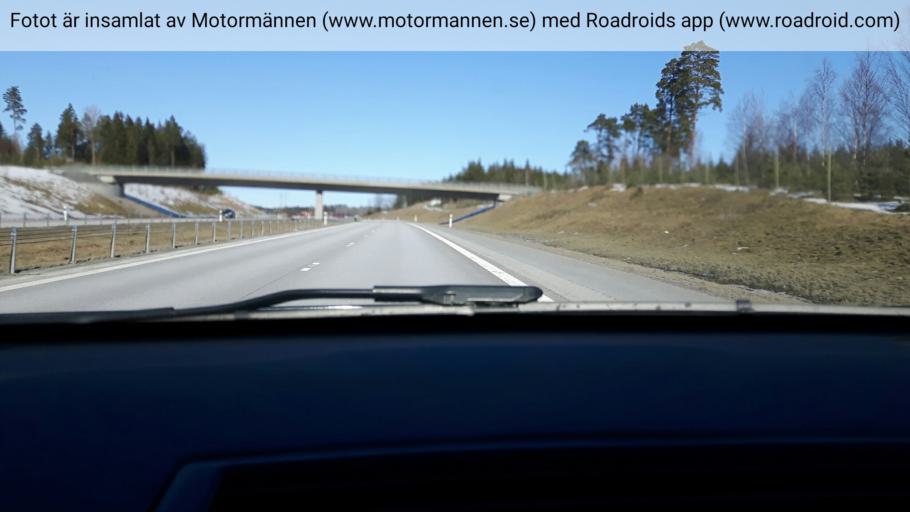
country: SE
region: Uppsala
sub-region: Uppsala Kommun
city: Storvreta
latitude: 59.9652
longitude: 17.6480
